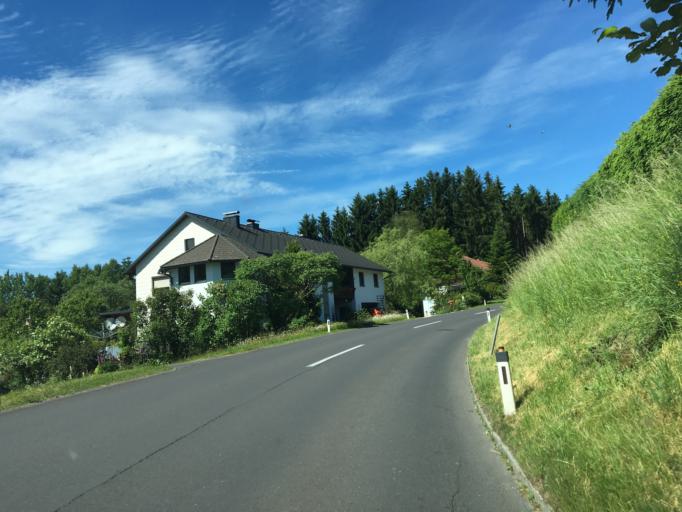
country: AT
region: Upper Austria
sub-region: Politischer Bezirk Urfahr-Umgebung
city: Zwettl an der Rodl
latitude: 48.4511
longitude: 14.2604
